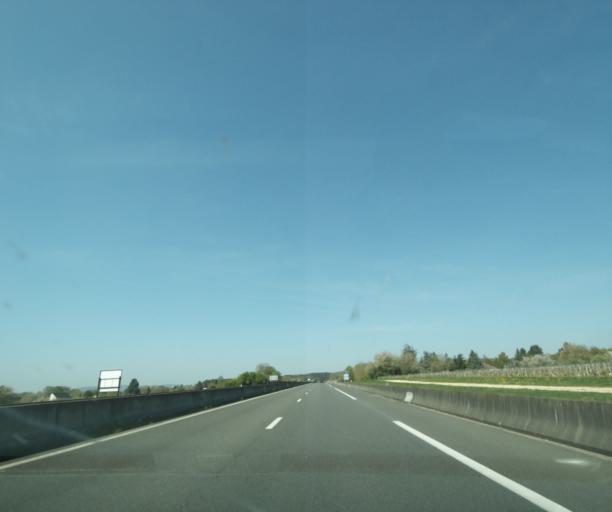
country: FR
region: Bourgogne
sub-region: Departement de la Nievre
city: Pouilly-sur-Loire
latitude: 47.2838
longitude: 2.9681
